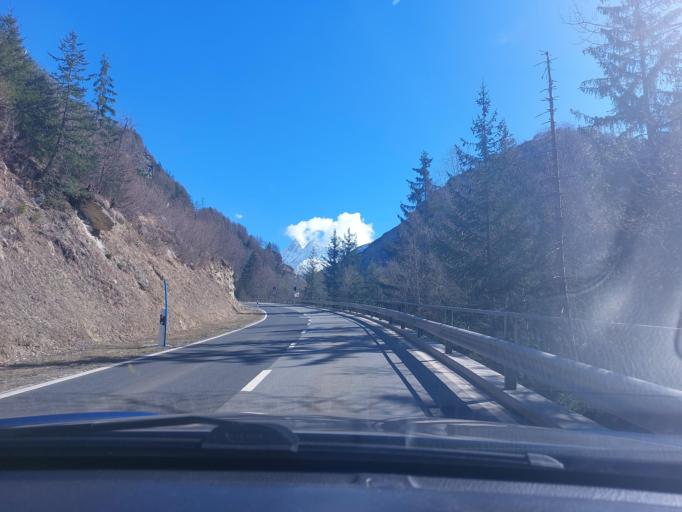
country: CH
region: Valais
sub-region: Herens District
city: Evolene
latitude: 46.1346
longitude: 7.4718
